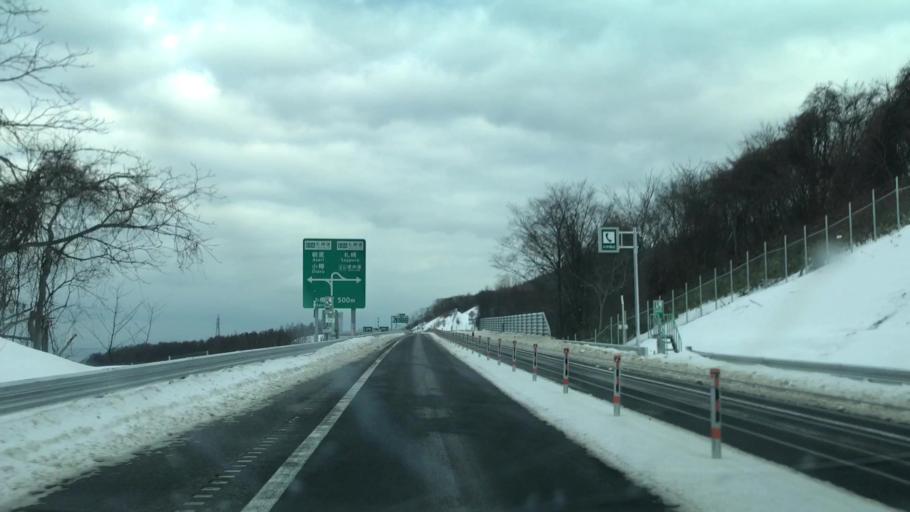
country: JP
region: Hokkaido
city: Otaru
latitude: 43.1596
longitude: 141.0531
